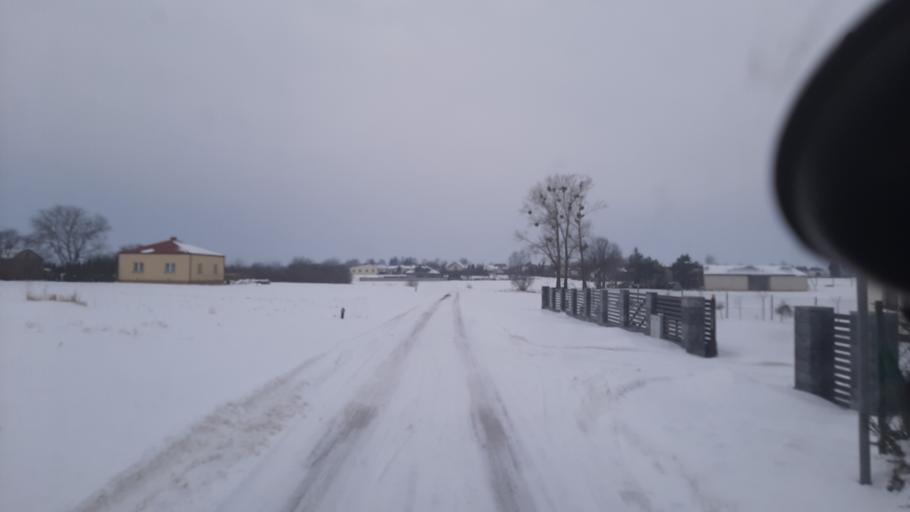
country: PL
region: Lublin Voivodeship
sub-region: Powiat lubelski
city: Garbow
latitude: 51.3565
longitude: 22.3840
